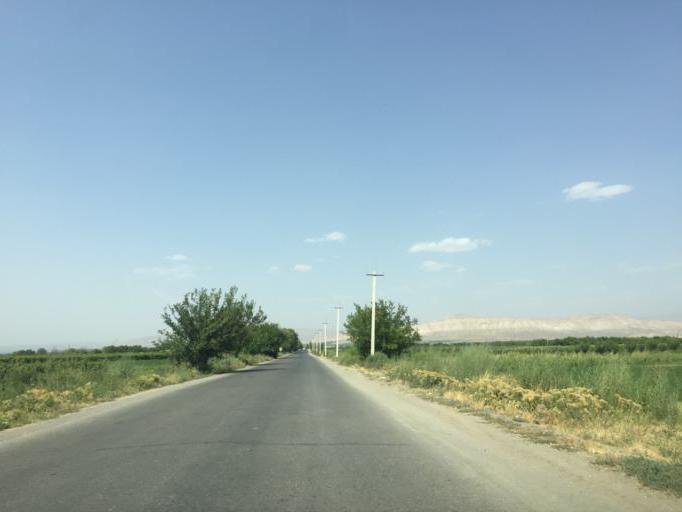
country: AM
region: Ararat
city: Vosketap'
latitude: 39.8849
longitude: 44.5916
